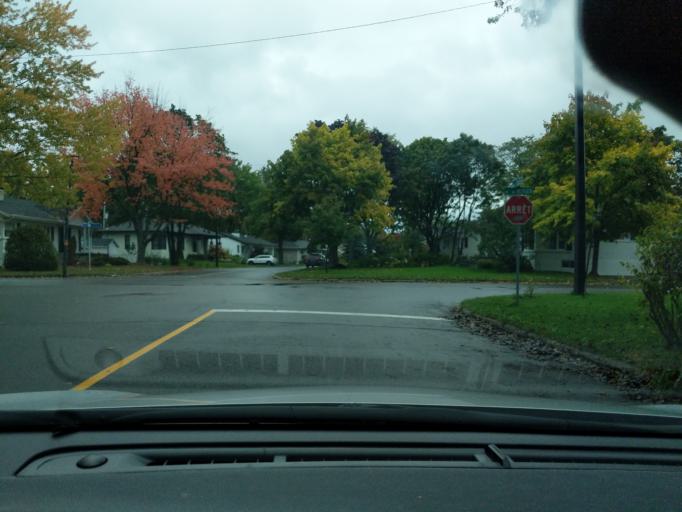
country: CA
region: Quebec
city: Quebec
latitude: 46.7645
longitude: -71.2695
